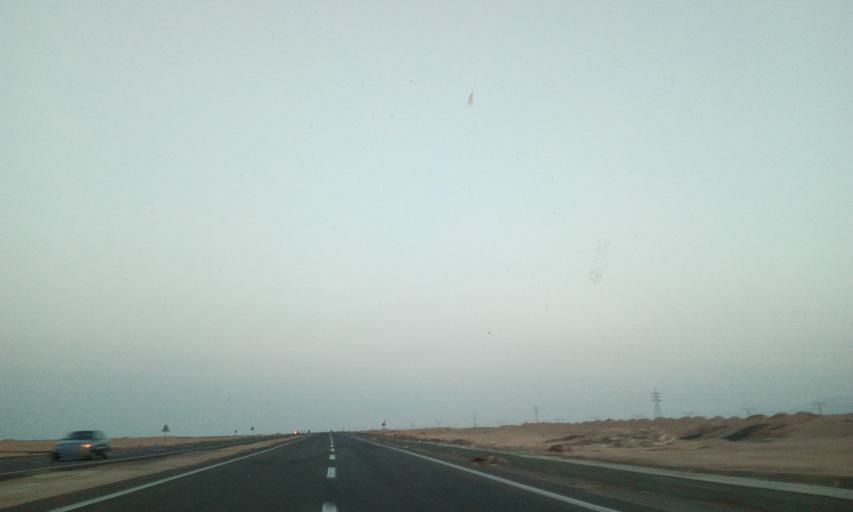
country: EG
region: Red Sea
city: El Gouna
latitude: 27.3540
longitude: 33.6464
